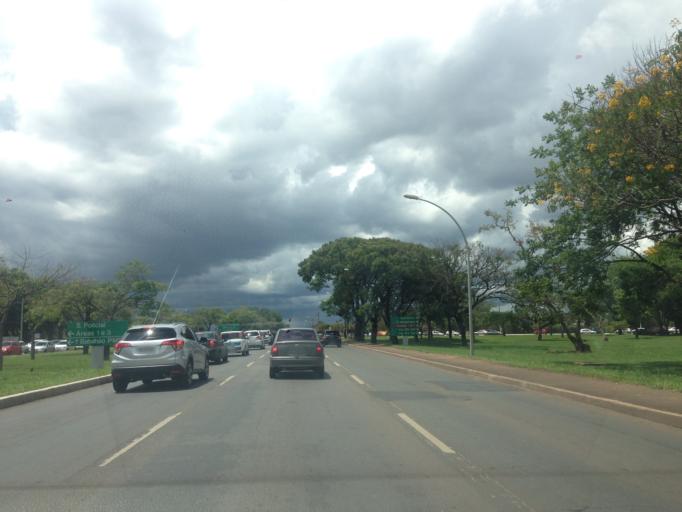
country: BR
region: Federal District
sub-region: Brasilia
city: Brasilia
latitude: -15.8264
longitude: -47.9325
